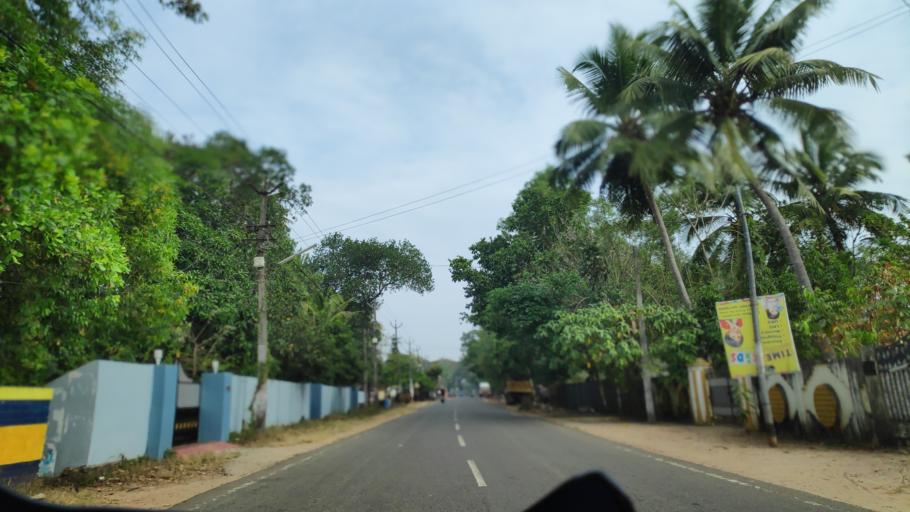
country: IN
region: Kerala
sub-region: Kottayam
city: Vaikam
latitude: 9.7489
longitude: 76.3634
